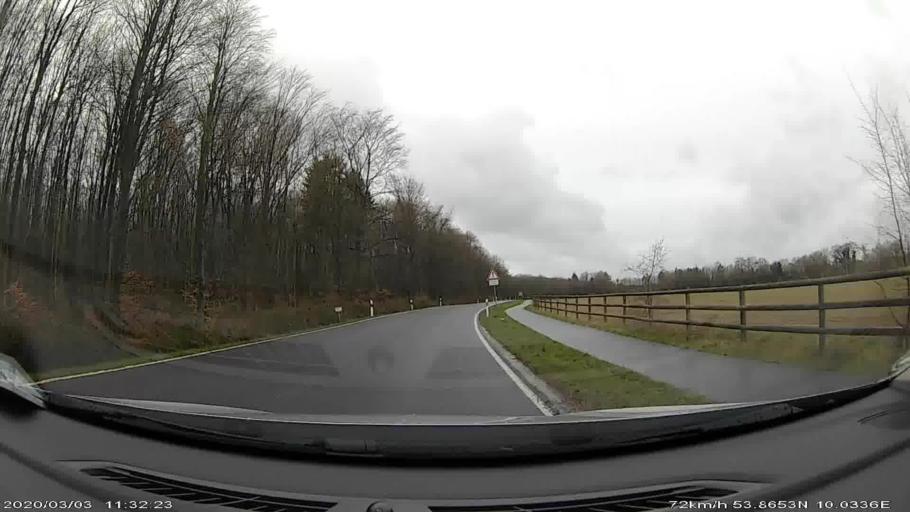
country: DE
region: Schleswig-Holstein
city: Kattendorf
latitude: 53.8653
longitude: 10.0287
